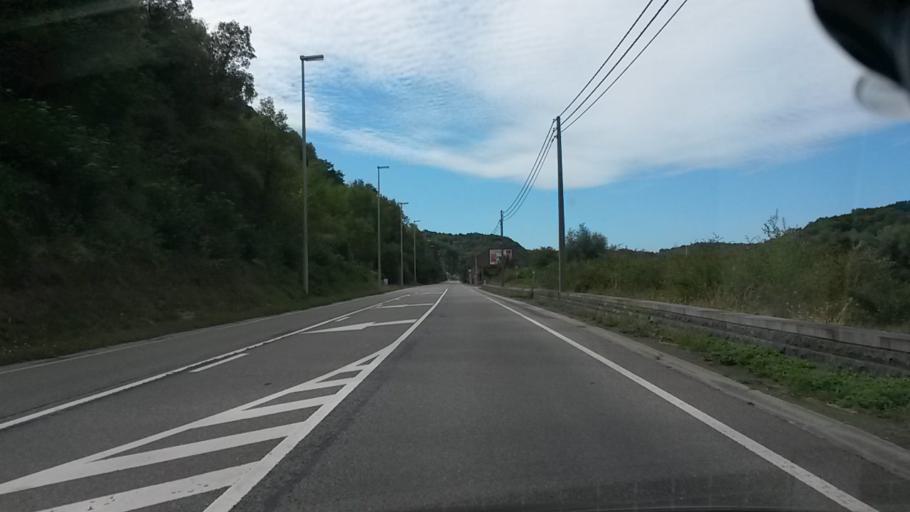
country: BE
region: Wallonia
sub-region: Province de Namur
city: Andenne
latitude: 50.4824
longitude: 5.0187
